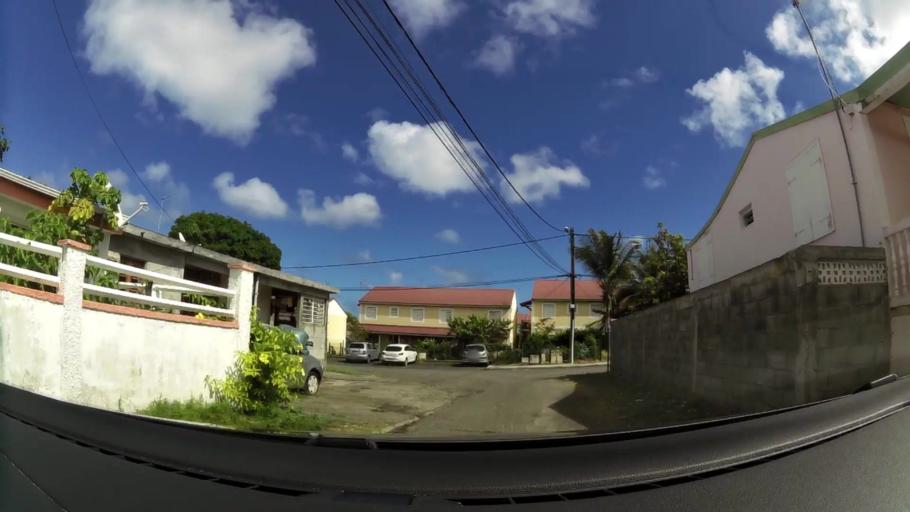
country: GP
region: Guadeloupe
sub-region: Guadeloupe
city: Anse-Bertrand
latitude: 16.4669
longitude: -61.5031
